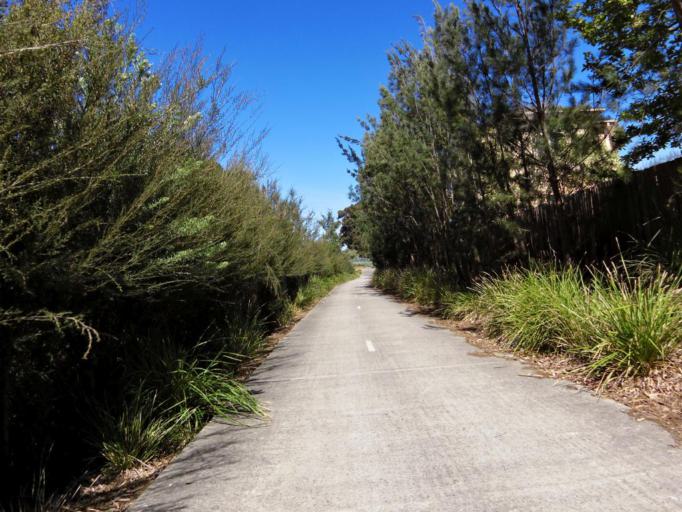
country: AU
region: Victoria
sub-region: Greater Dandenong
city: Dandenong North
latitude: -37.9690
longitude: 145.1939
